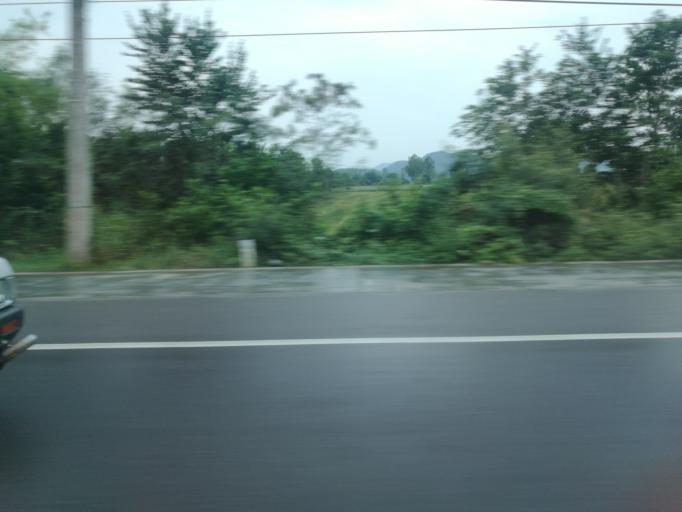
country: TH
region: Prachuap Khiri Khan
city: Kui Buri
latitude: 12.1149
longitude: 99.8530
